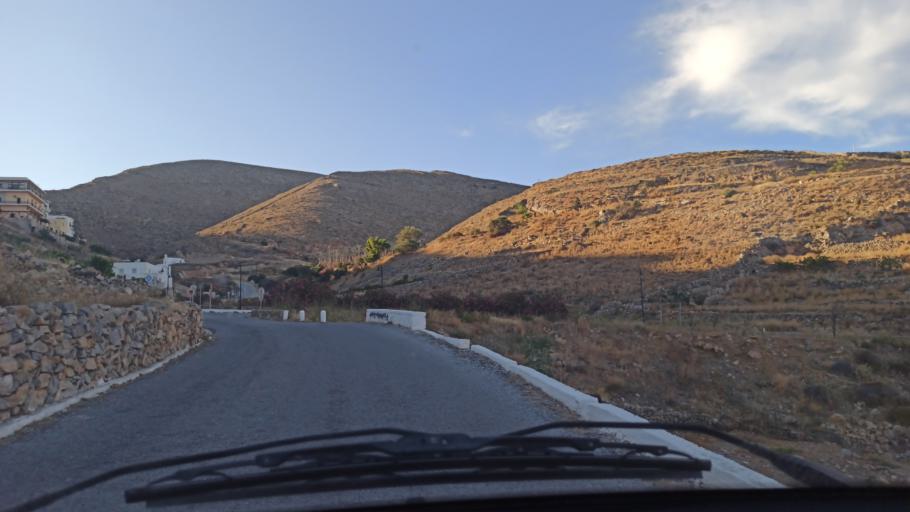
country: GR
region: South Aegean
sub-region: Nomos Kykladon
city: Ano Syros
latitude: 37.4506
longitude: 24.9375
